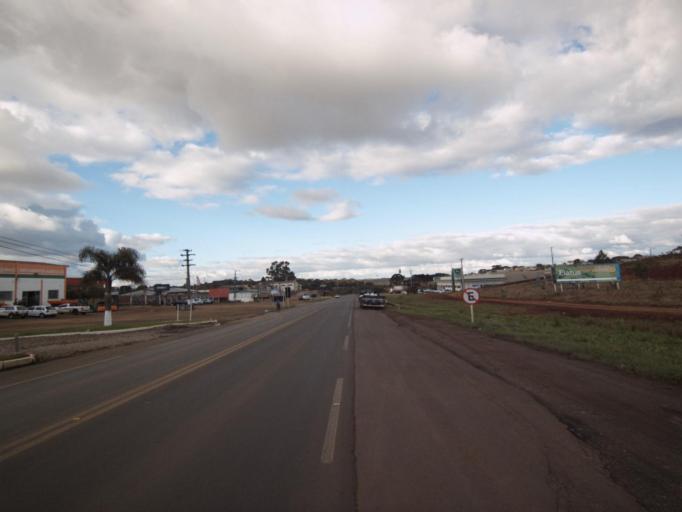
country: BR
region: Santa Catarina
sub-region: Campos Novos
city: Campos Novos
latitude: -27.3895
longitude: -51.2116
